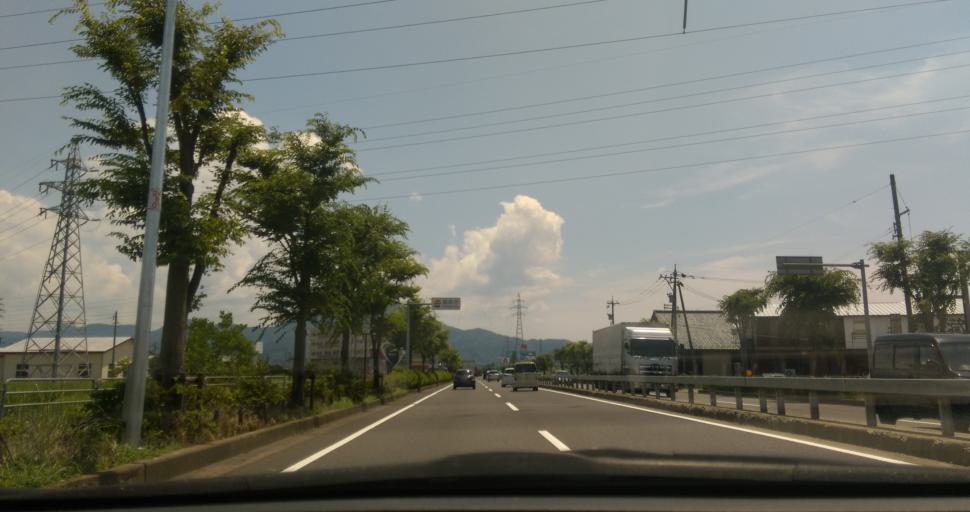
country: JP
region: Fukui
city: Sabae
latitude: 35.9310
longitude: 136.1899
